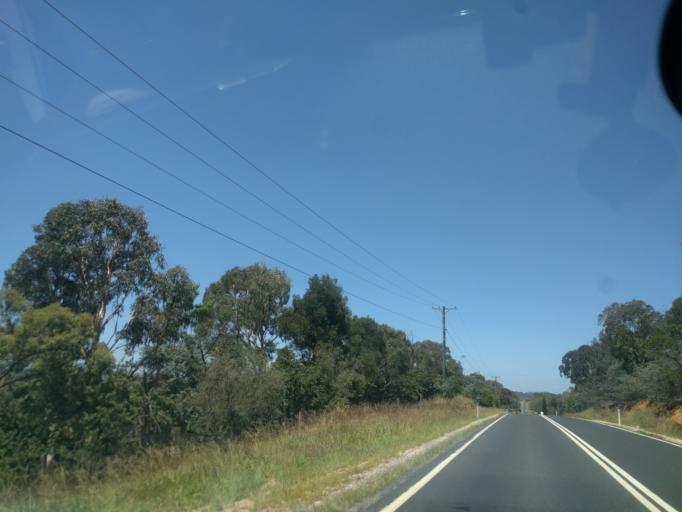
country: AU
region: New South Wales
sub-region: Armidale Dumaresq
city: Armidale
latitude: -30.5244
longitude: 151.6931
